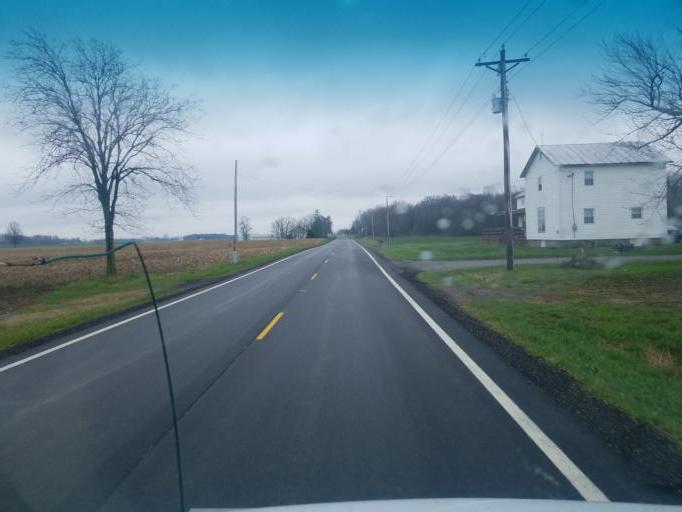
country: US
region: Ohio
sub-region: Huron County
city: Willard
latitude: 40.9601
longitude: -82.8094
